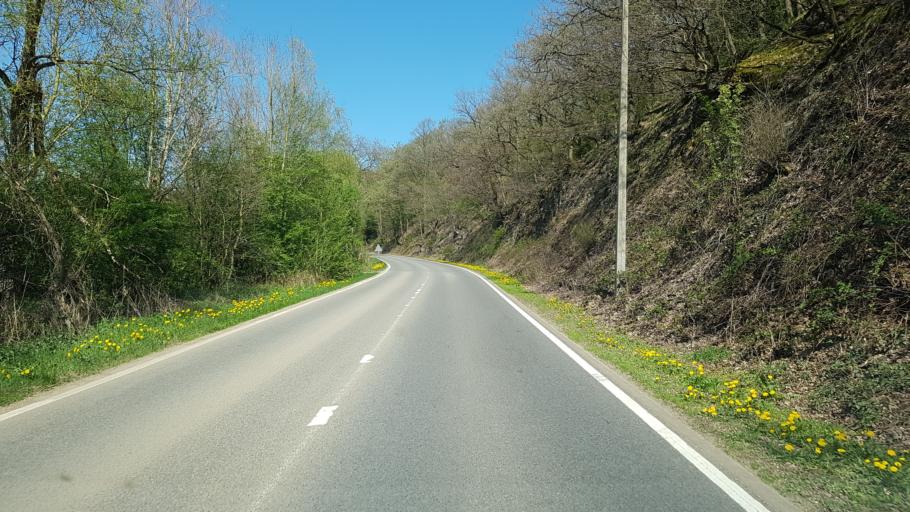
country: BE
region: Wallonia
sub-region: Province de Liege
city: Plombieres
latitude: 50.7387
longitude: 5.9691
